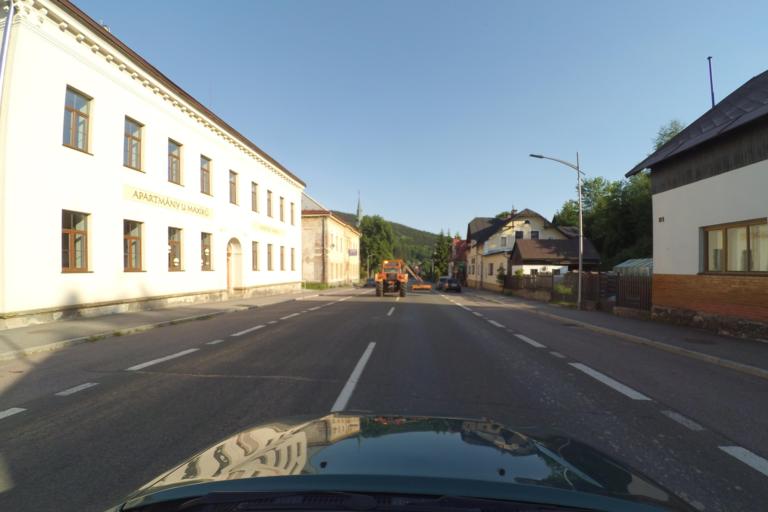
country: CZ
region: Kralovehradecky
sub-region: Okres Trutnov
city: Svoboda nad Upou
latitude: 50.6587
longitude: 15.8194
